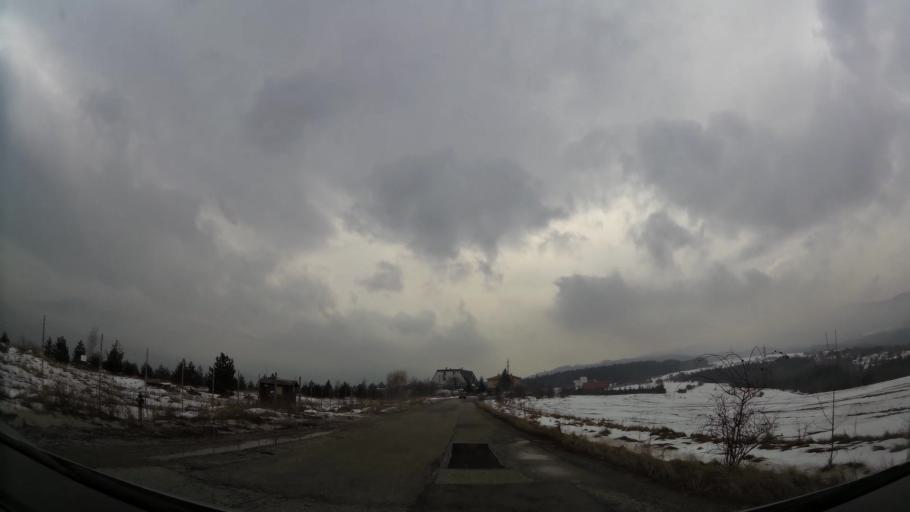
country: BG
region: Sofiya
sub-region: Obshtina Bozhurishte
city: Bozhurishte
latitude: 42.6690
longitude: 23.2197
